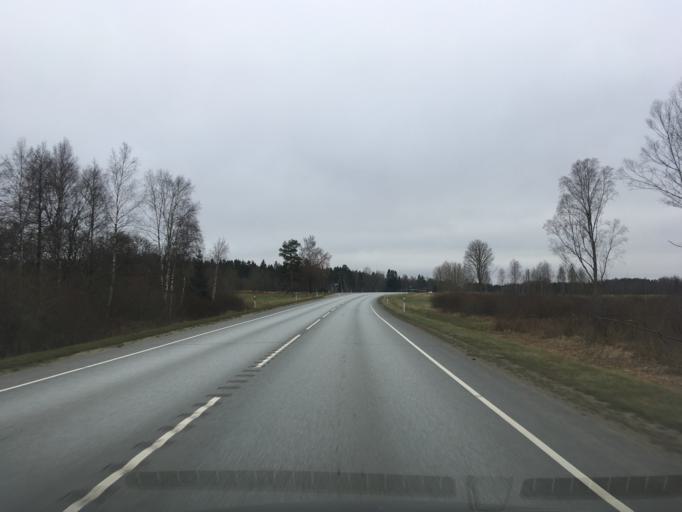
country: EE
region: Laeaene-Virumaa
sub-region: Viru-Nigula vald
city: Kunda
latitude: 59.4149
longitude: 26.6520
